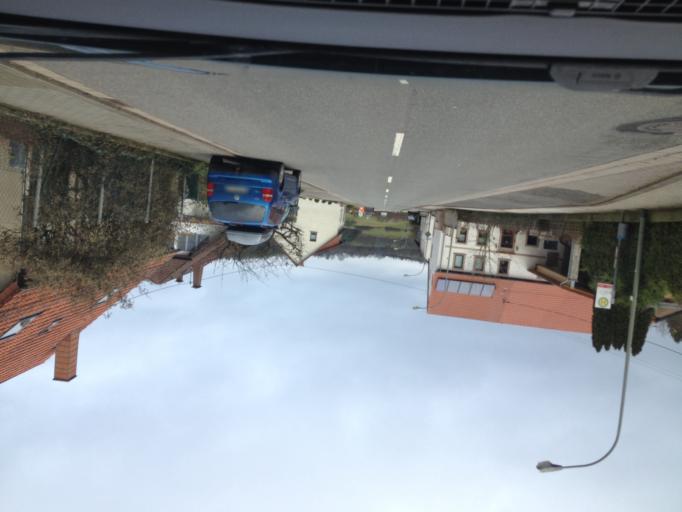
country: DE
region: Rheinland-Pfalz
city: Breitenbach
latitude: 49.4513
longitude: 7.2301
